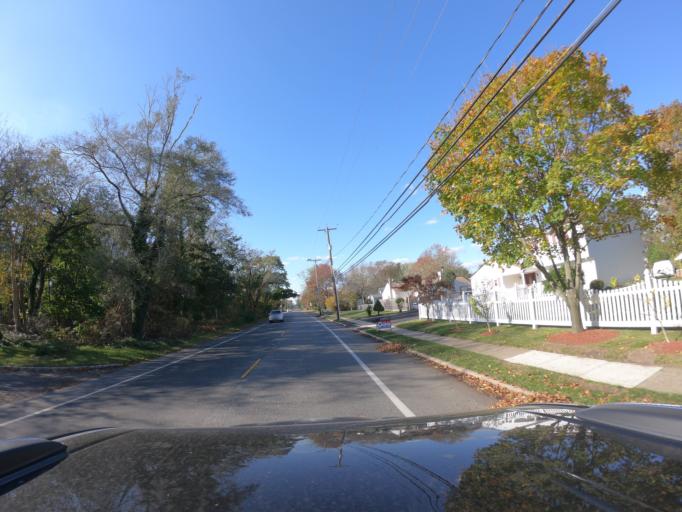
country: US
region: New Jersey
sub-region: Monmouth County
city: Ramtown
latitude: 40.0964
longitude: -74.1620
